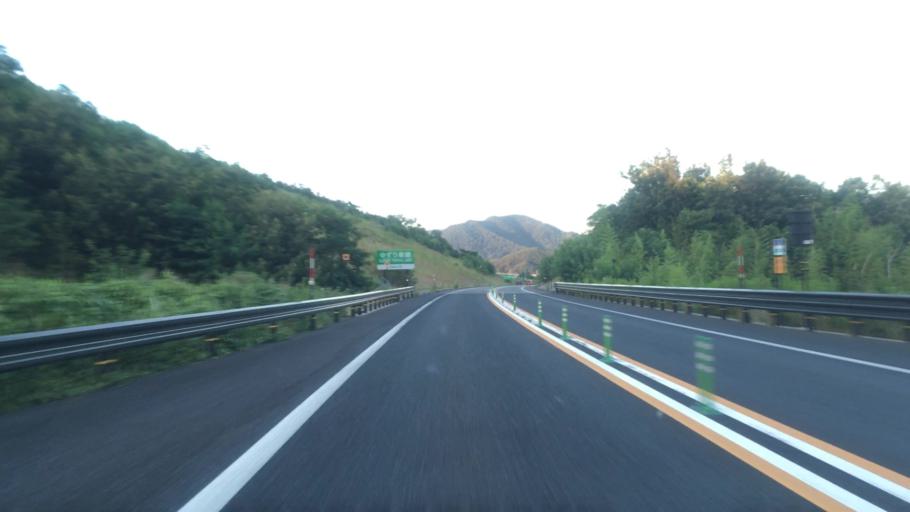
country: JP
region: Tottori
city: Tottori
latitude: 35.5481
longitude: 134.2648
